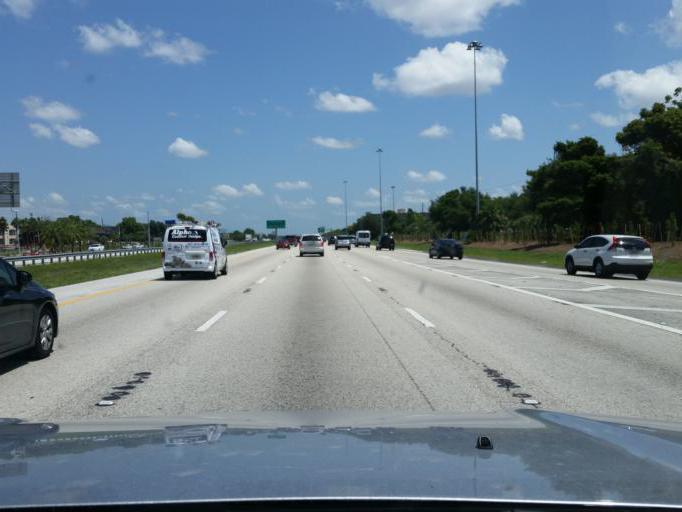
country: US
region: Florida
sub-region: Orange County
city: Doctor Phillips
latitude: 28.4241
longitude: -81.4741
